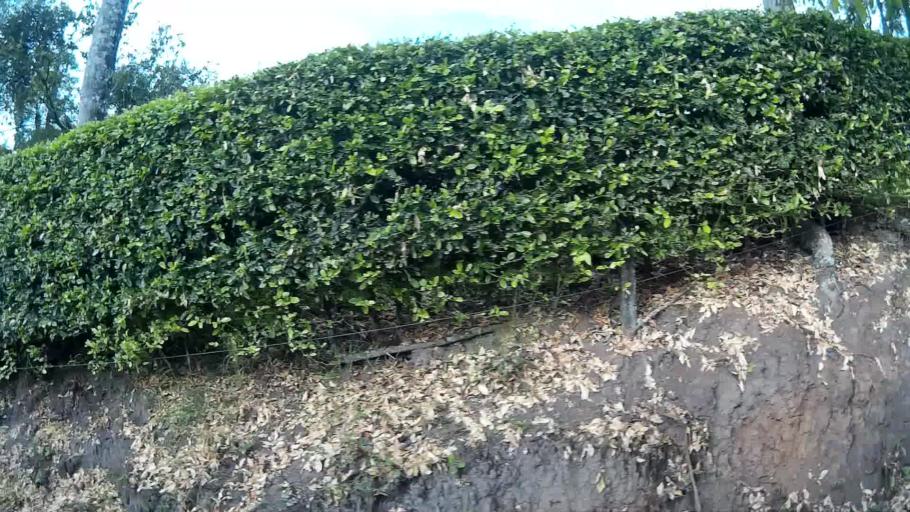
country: CO
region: Valle del Cauca
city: Ulloa
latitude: 4.7304
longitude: -75.7291
